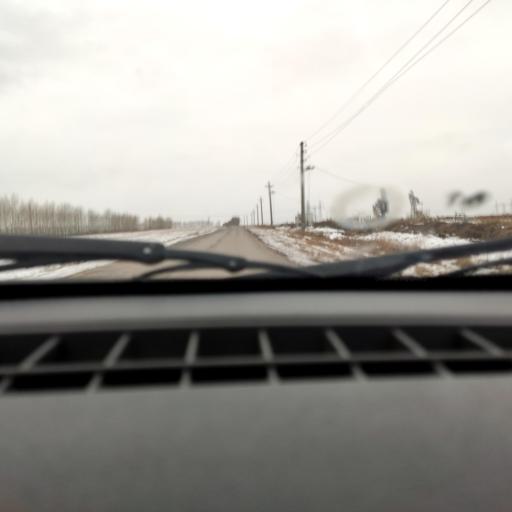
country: RU
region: Bashkortostan
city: Tolbazy
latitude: 54.2484
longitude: 55.8929
